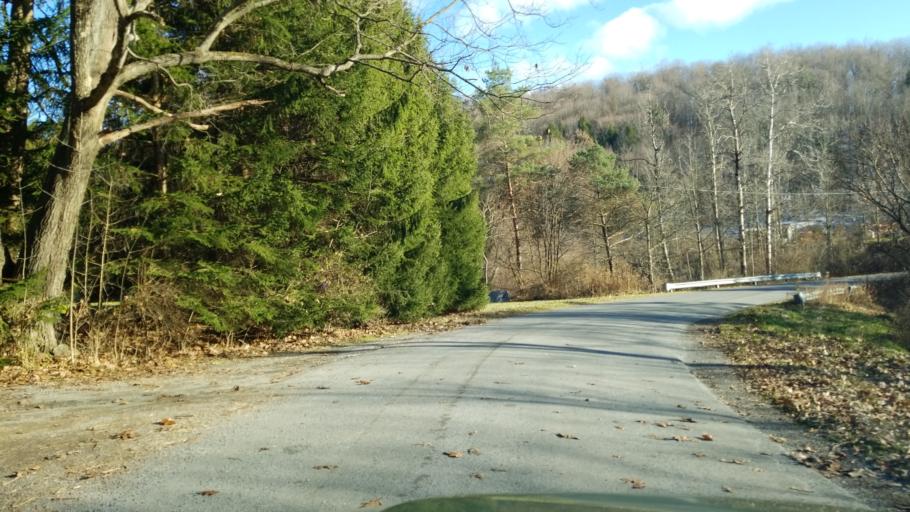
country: US
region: Pennsylvania
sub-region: Jefferson County
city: Brockway
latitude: 41.2590
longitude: -78.7987
